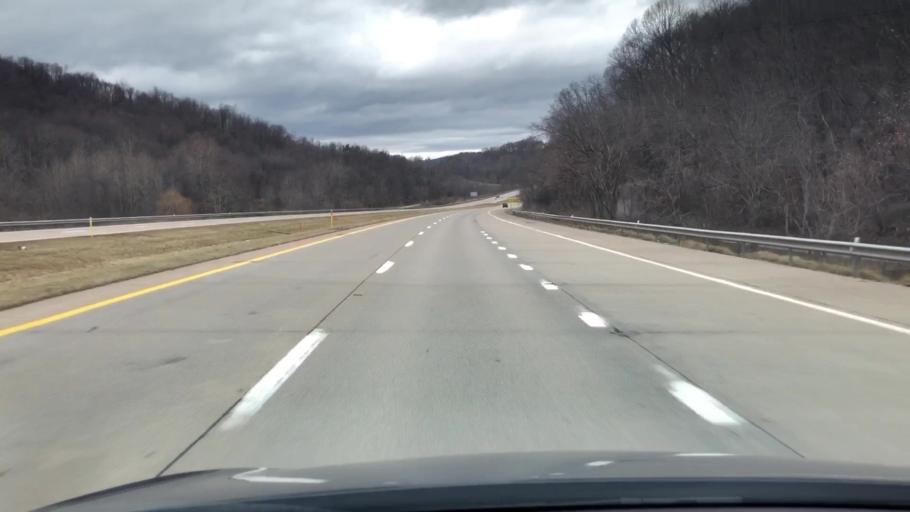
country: US
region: Pennsylvania
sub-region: Westmoreland County
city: New Stanton
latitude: 40.2063
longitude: -79.5855
